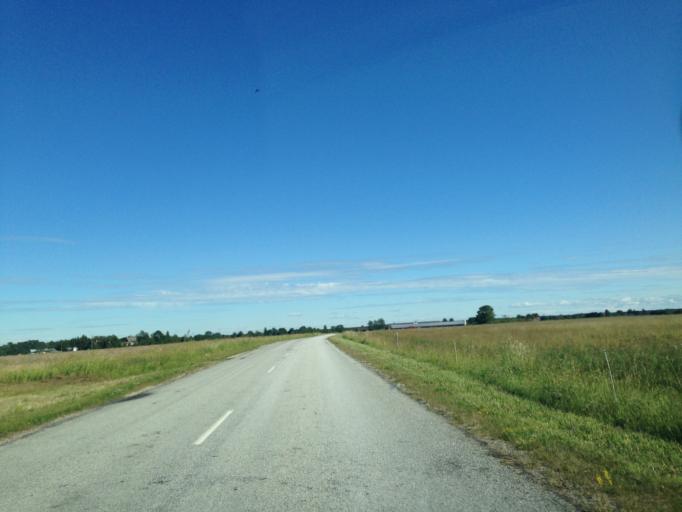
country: EE
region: Harju
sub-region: Kuusalu vald
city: Kuusalu
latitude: 59.4629
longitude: 25.3330
